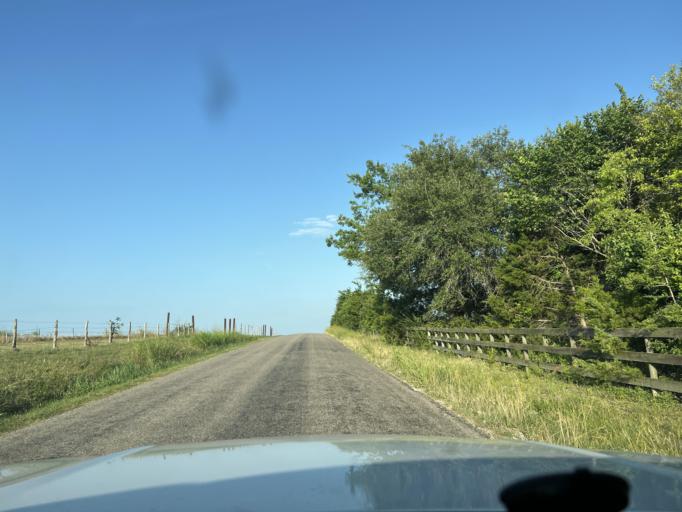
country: US
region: Texas
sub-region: Washington County
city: Brenham
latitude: 30.2297
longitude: -96.3853
